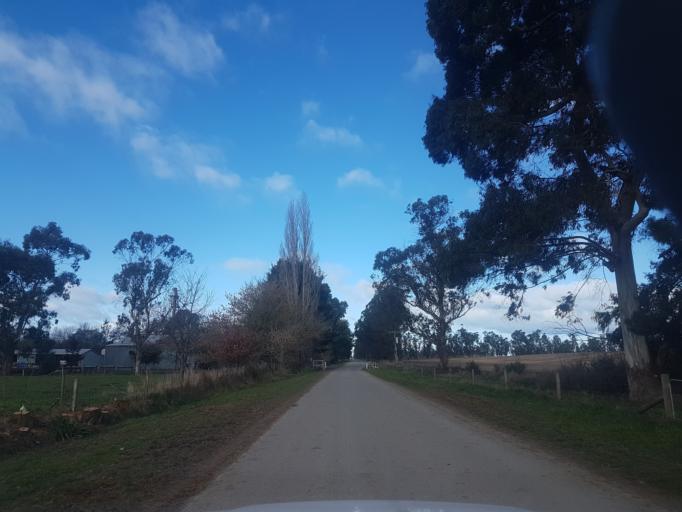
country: NZ
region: Canterbury
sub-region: Timaru District
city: Pleasant Point
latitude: -44.2071
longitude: 171.2070
